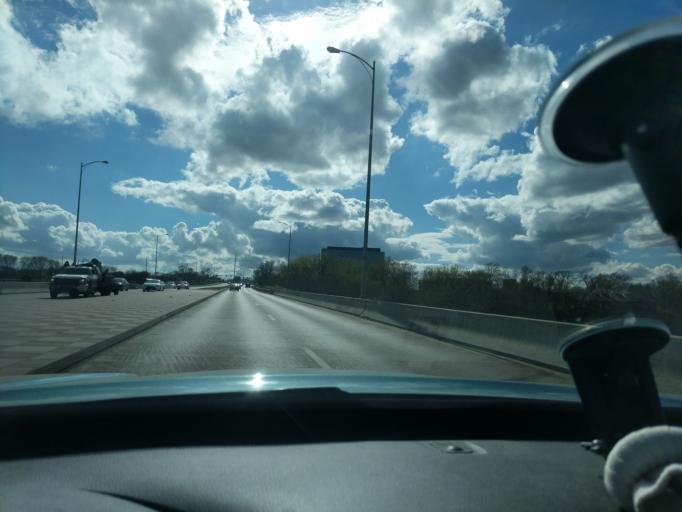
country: US
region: Nebraska
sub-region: Douglas County
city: Ralston
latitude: 41.2370
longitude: -96.0163
